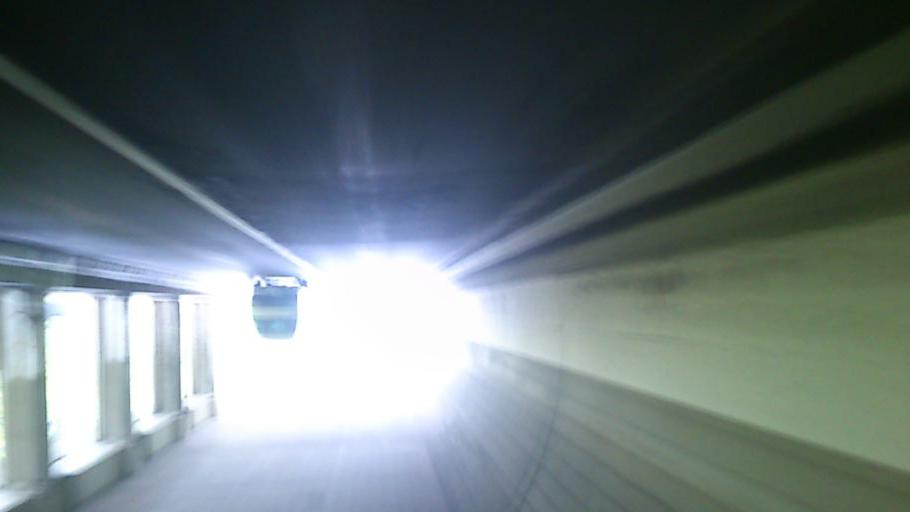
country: JP
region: Hokkaido
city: Kamikawa
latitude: 43.7426
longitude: 142.9353
